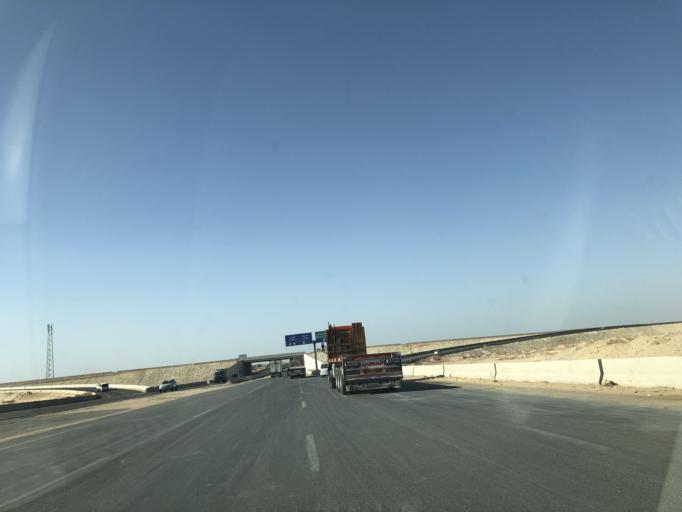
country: EG
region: Muhafazat al Minufiyah
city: Ashmun
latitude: 30.0646
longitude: 30.8459
